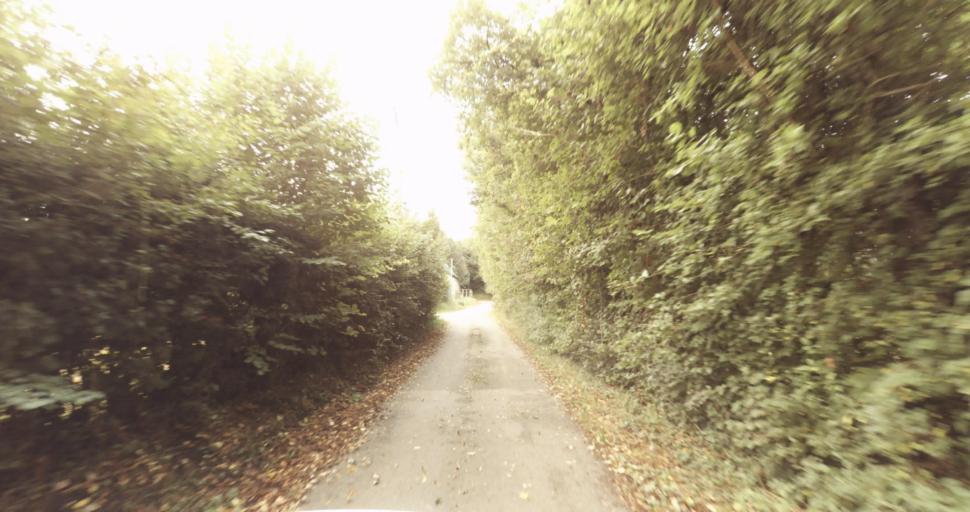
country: FR
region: Lower Normandy
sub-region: Departement de l'Orne
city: Trun
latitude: 48.9164
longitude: 0.0930
